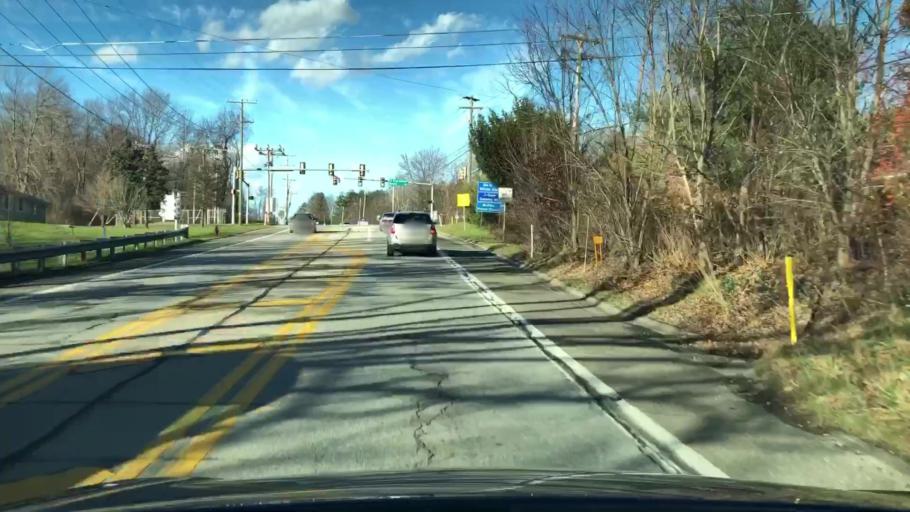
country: US
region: Pennsylvania
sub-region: Butler County
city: Saxonburg
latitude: 40.7233
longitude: -79.7564
